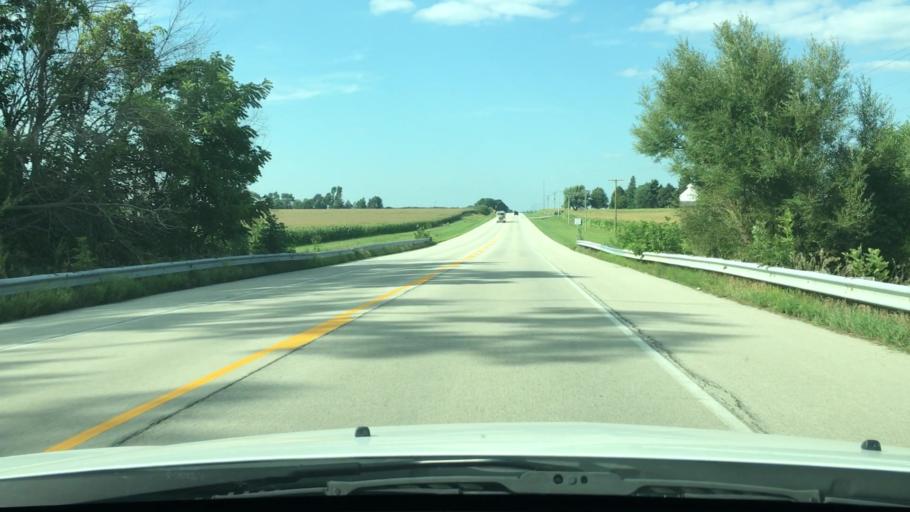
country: US
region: Illinois
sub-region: DeKalb County
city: Waterman
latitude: 41.7771
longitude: -88.7542
